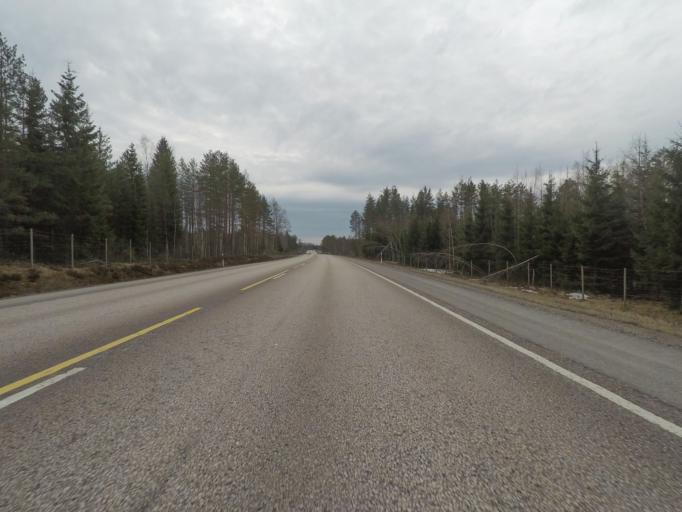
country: FI
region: Central Finland
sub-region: Joutsa
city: Leivonmaeki
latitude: 61.8318
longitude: 26.0964
